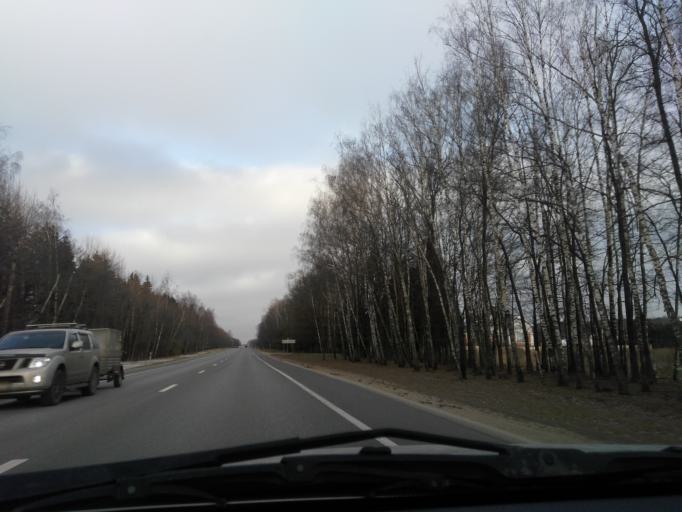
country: RU
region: Moskovskaya
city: Troitsk
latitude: 55.2953
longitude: 37.1331
